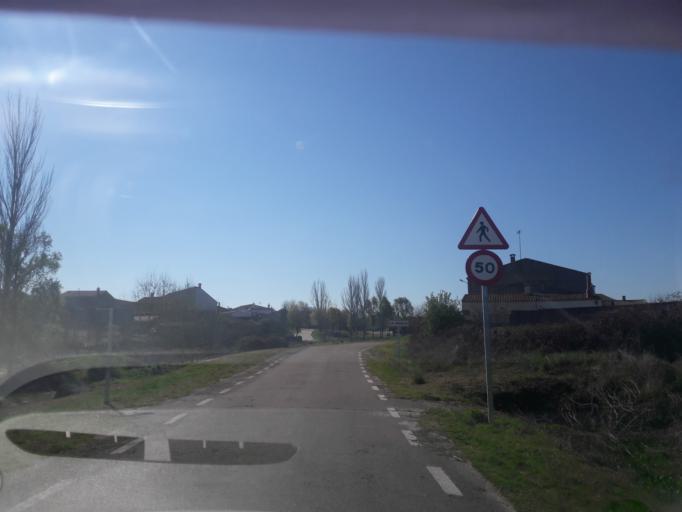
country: ES
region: Castille and Leon
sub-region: Provincia de Salamanca
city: Valsalabroso
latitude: 41.1566
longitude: -6.4888
